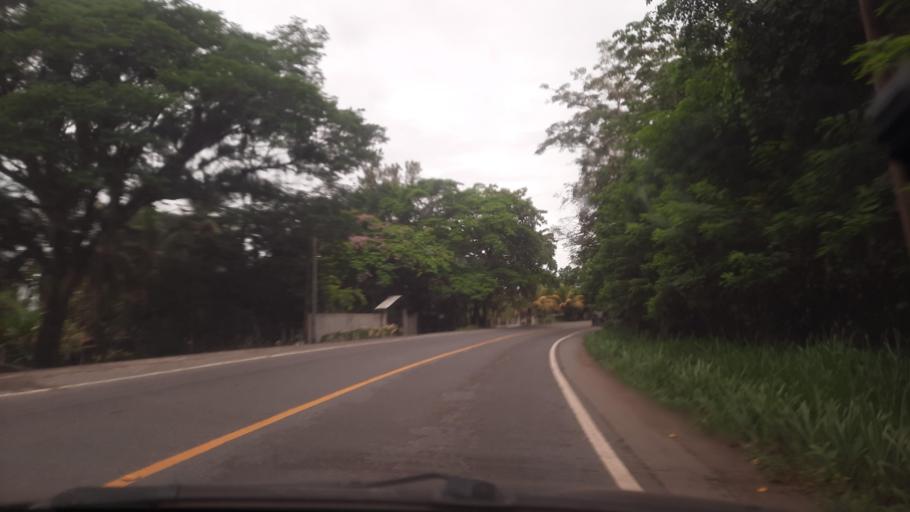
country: GT
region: Izabal
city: Morales
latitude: 15.4648
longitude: -88.9103
